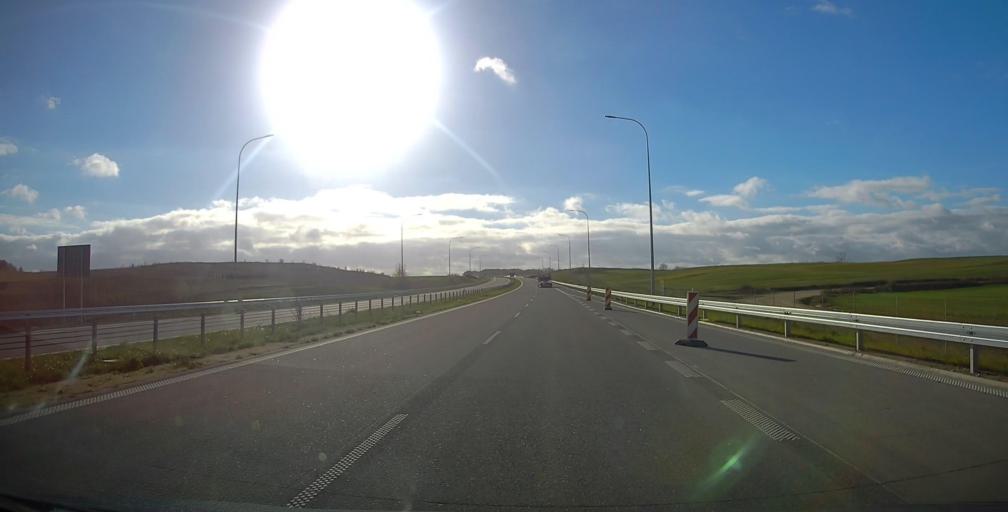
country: PL
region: Warmian-Masurian Voivodeship
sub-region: Powiat elcki
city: Elk
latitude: 53.7408
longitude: 22.2957
